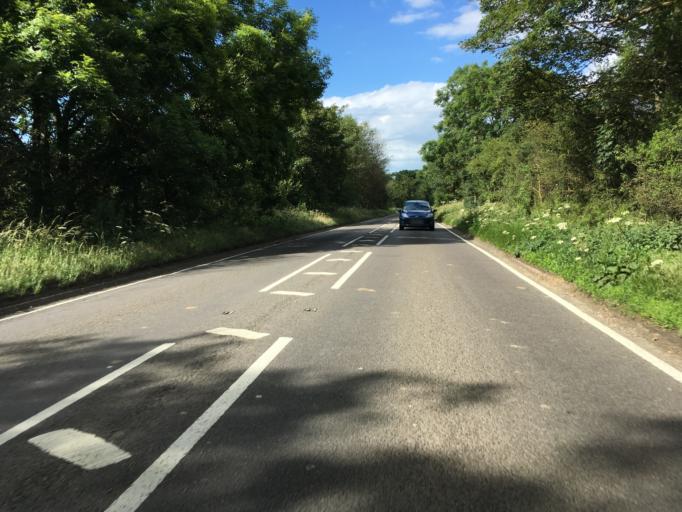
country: GB
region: England
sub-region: Buckinghamshire
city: Stewkley
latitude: 51.8710
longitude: -0.7544
